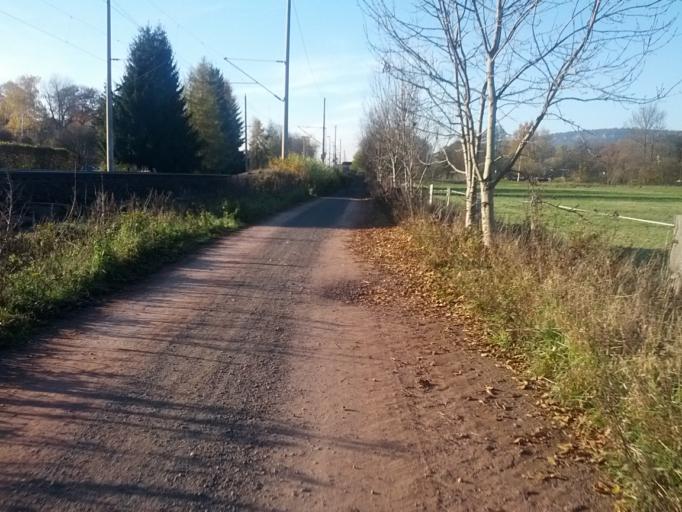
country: DE
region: Thuringia
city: Seebach
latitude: 50.9443
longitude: 10.4327
